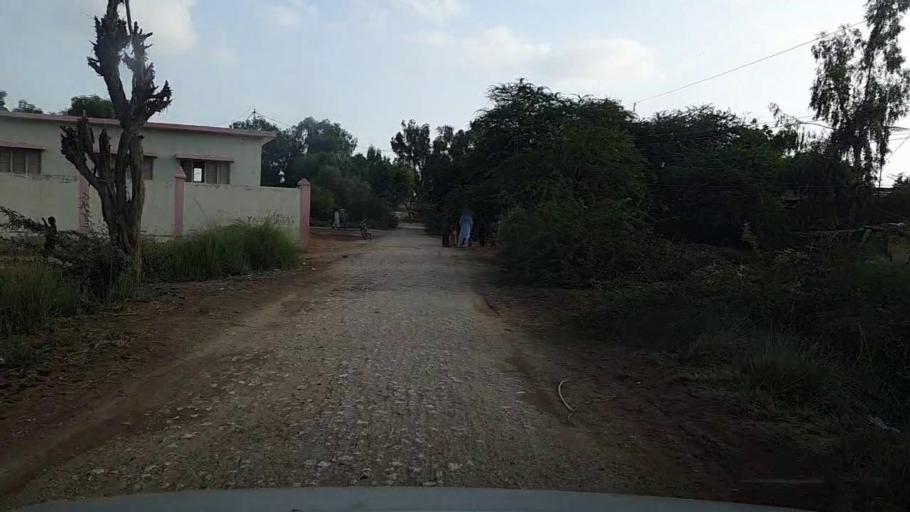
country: PK
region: Sindh
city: Pad Idan
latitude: 26.7895
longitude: 68.2220
